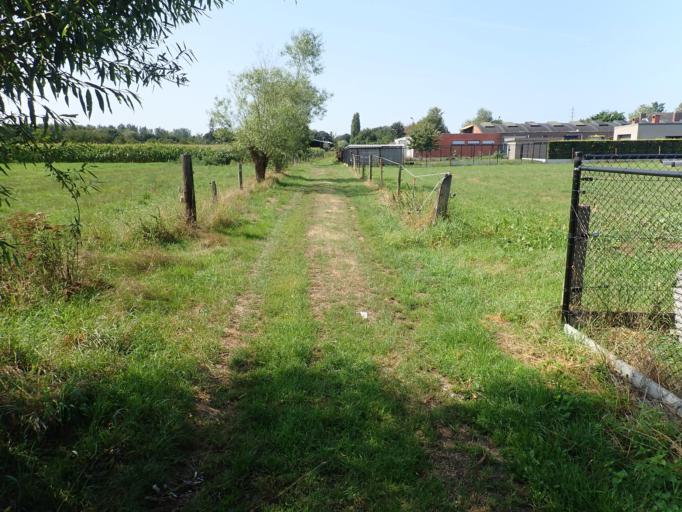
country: BE
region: Flanders
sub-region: Provincie Oost-Vlaanderen
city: Buggenhout
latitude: 51.0318
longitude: 4.2010
